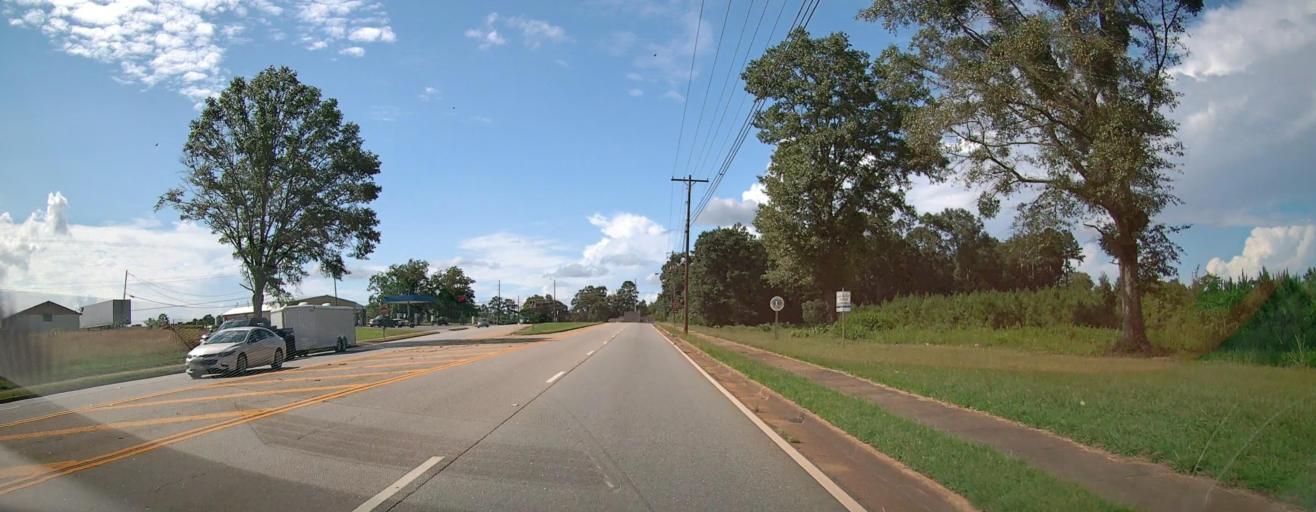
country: US
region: Georgia
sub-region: Upson County
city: Thomaston
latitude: 32.8728
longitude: -84.3239
